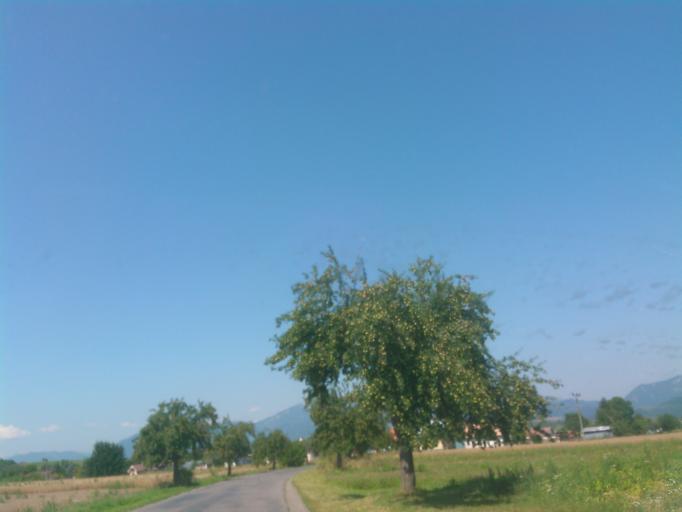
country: SK
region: Zilinsky
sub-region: Okres Liptovsky Mikulas
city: Liptovsky Mikulas
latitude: 49.0475
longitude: 19.4869
